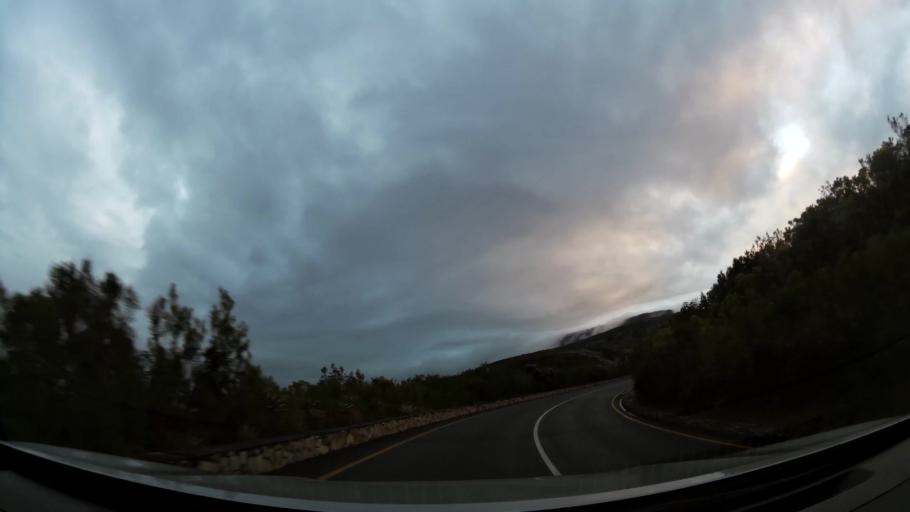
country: ZA
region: Western Cape
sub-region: Overberg District Municipality
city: Swellendam
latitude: -33.9874
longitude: 20.7102
